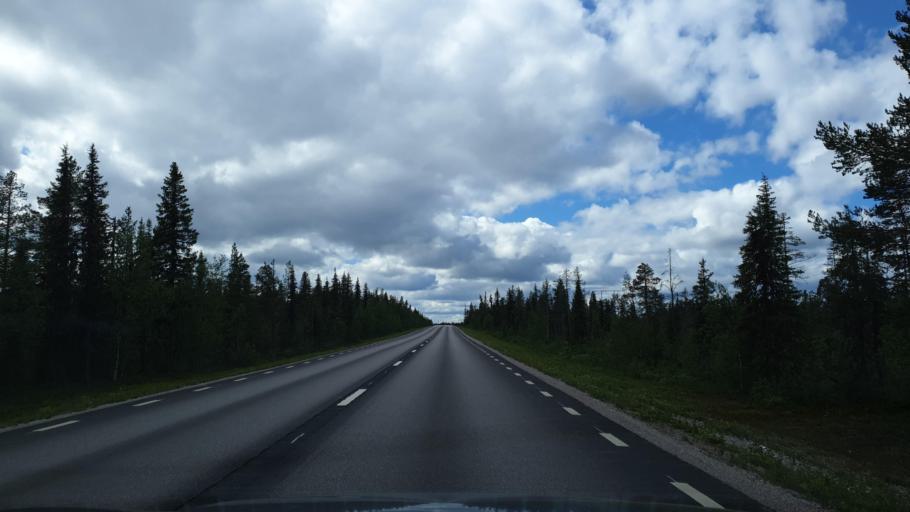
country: SE
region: Norrbotten
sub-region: Gallivare Kommun
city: Gaellivare
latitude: 67.0669
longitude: 20.2694
